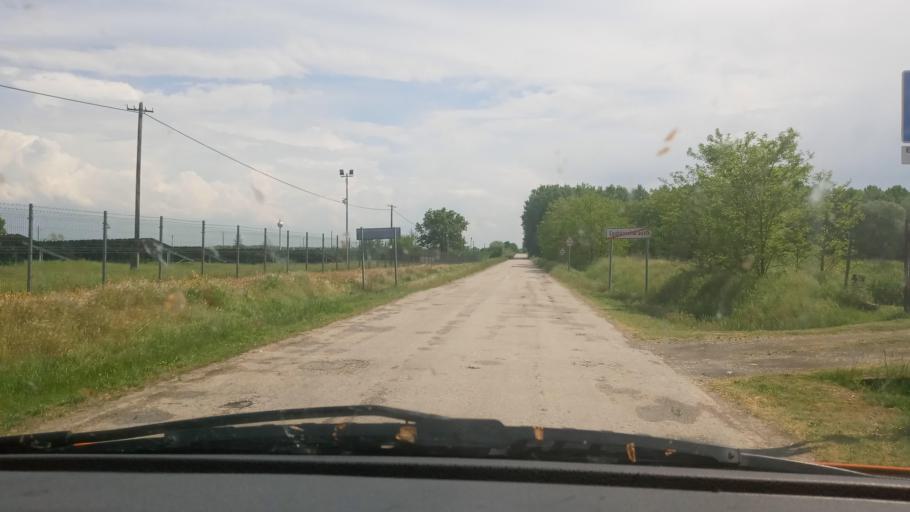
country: HU
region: Baranya
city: Siklos
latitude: 45.8120
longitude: 18.3394
